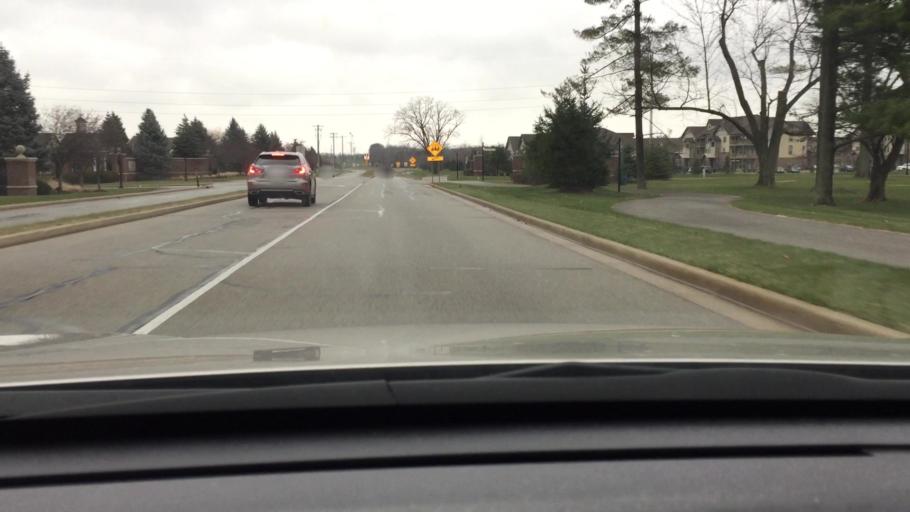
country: US
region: Indiana
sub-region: Hamilton County
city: Carmel
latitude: 40.0075
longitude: -86.0966
